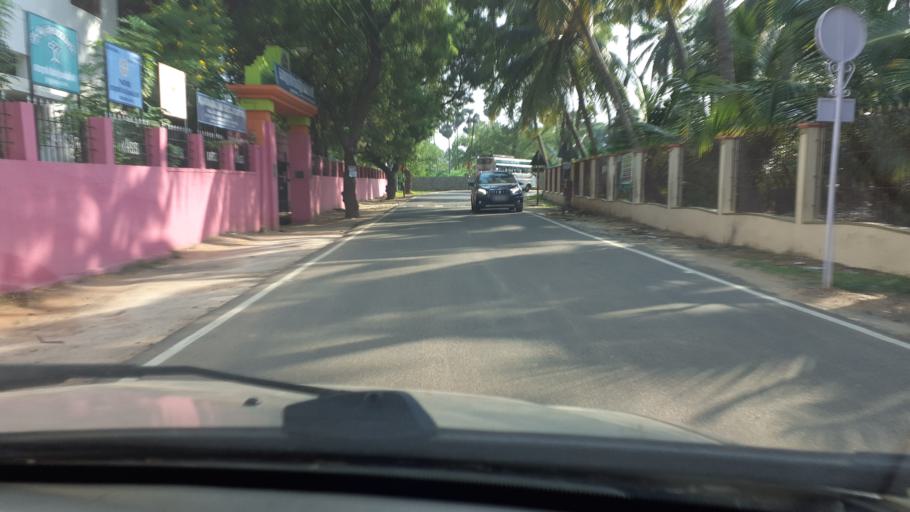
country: IN
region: Tamil Nadu
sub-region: Thoothukkudi
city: Eral
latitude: 8.5844
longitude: 78.0372
